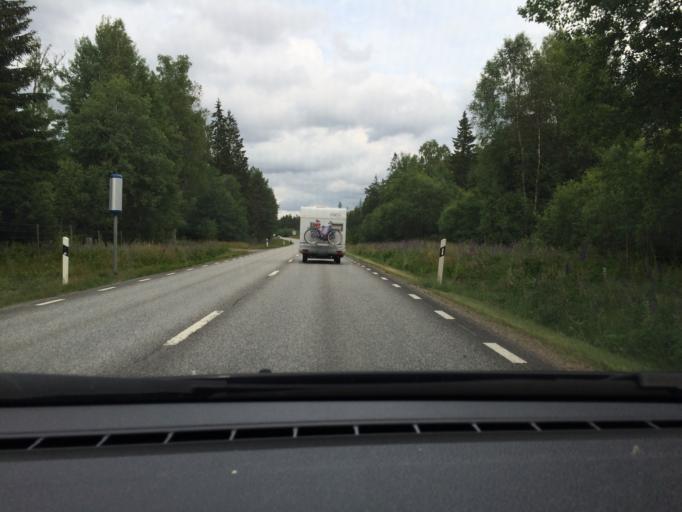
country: SE
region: Joenkoeping
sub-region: Varnamo Kommun
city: Forsheda
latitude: 57.1628
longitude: 13.8692
